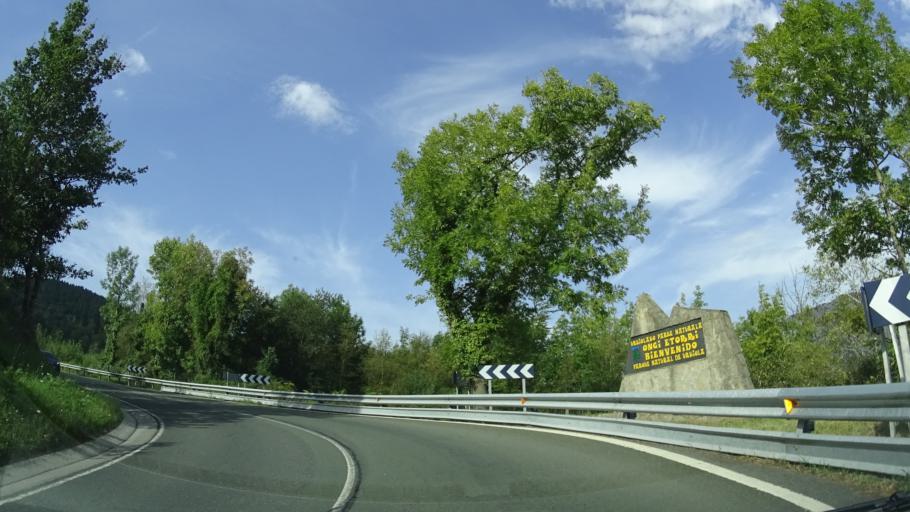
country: ES
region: Basque Country
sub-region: Bizkaia
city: Manaria
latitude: 43.1106
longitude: -2.6462
